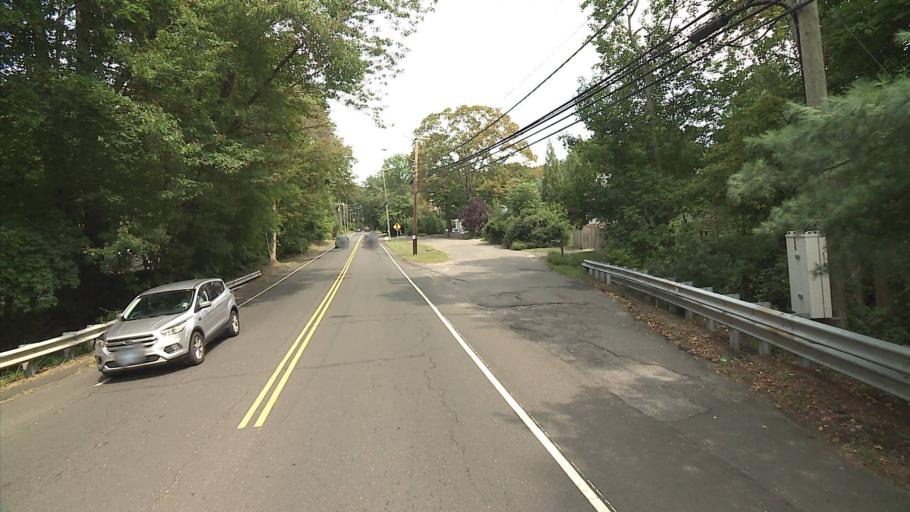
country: US
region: Connecticut
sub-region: Fairfield County
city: North Stamford
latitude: 41.1237
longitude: -73.5445
